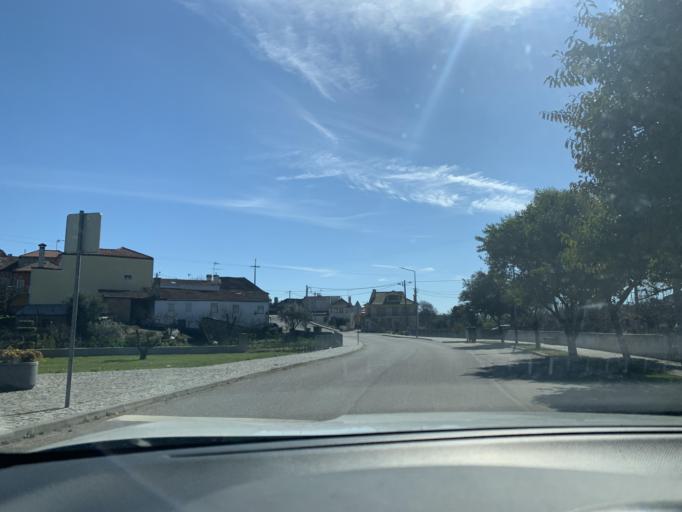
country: PT
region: Viseu
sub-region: Concelho de Tondela
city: Tondela
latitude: 40.5887
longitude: -8.0258
